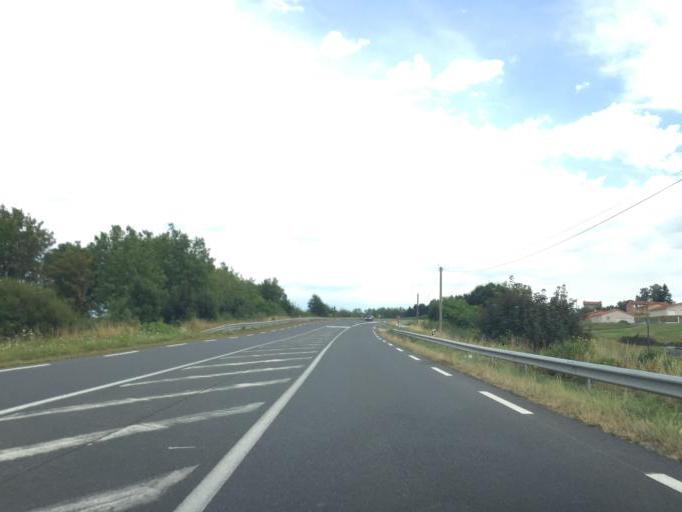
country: FR
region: Rhone-Alpes
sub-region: Departement de la Loire
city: Saint-Symphorien-de-Lay
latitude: 45.9519
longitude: 4.1951
